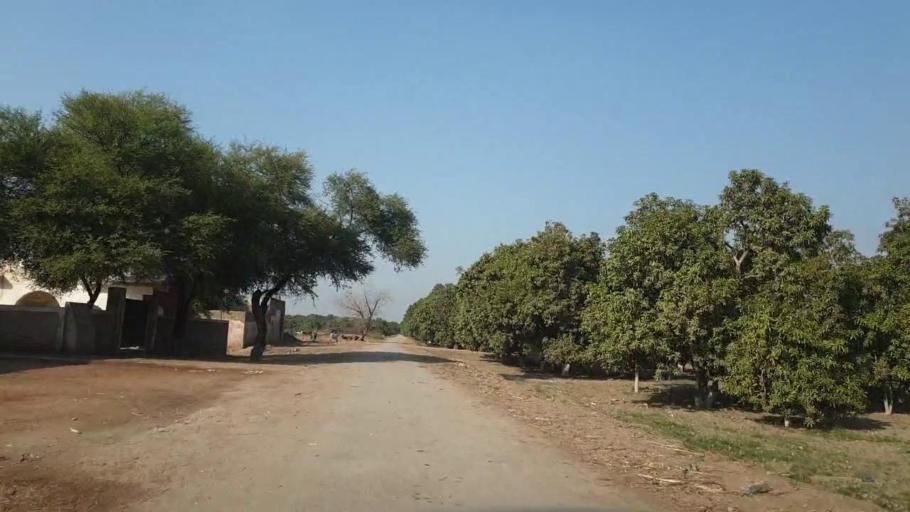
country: PK
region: Sindh
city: Tando Allahyar
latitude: 25.5697
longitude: 68.6721
